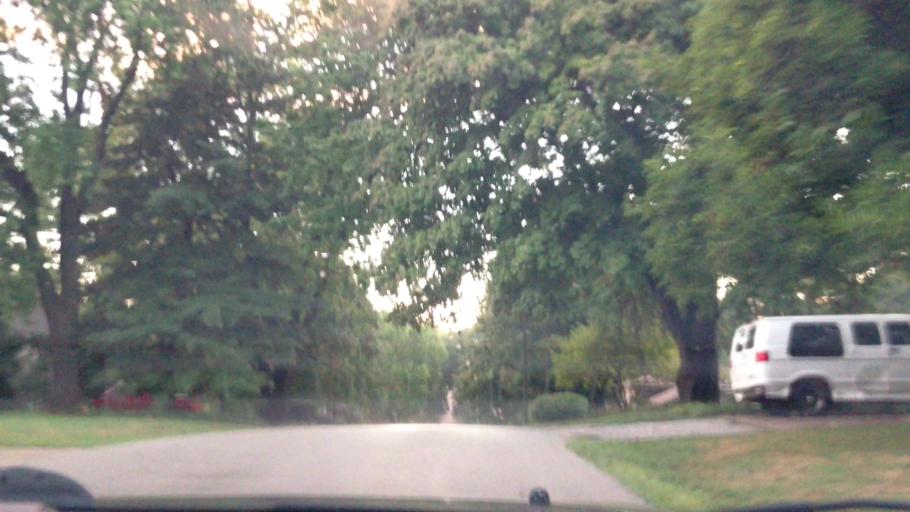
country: US
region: Missouri
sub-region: Clay County
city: Gladstone
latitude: 39.2428
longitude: -94.5797
